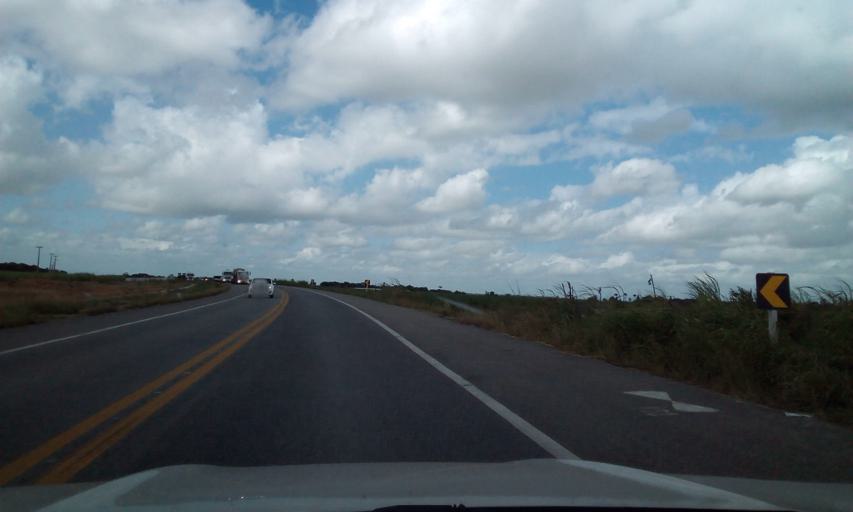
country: BR
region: Alagoas
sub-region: Pilar
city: Pilar
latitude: -9.5836
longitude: -35.9743
